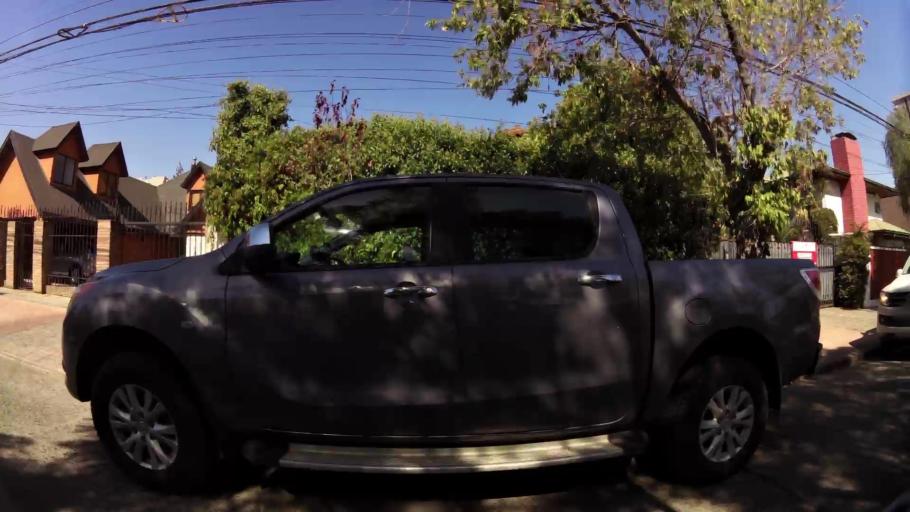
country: CL
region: Maule
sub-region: Provincia de Talca
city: Talca
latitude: -35.4198
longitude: -71.6632
